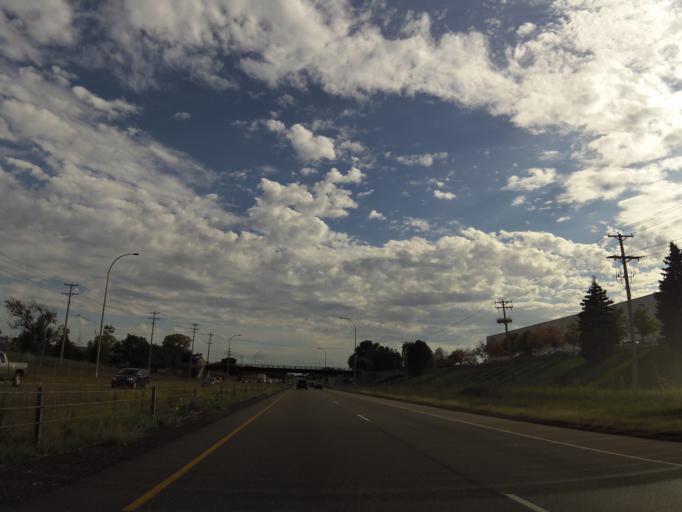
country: US
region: Minnesota
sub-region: Hennepin County
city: New Hope
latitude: 45.0508
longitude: -93.4010
